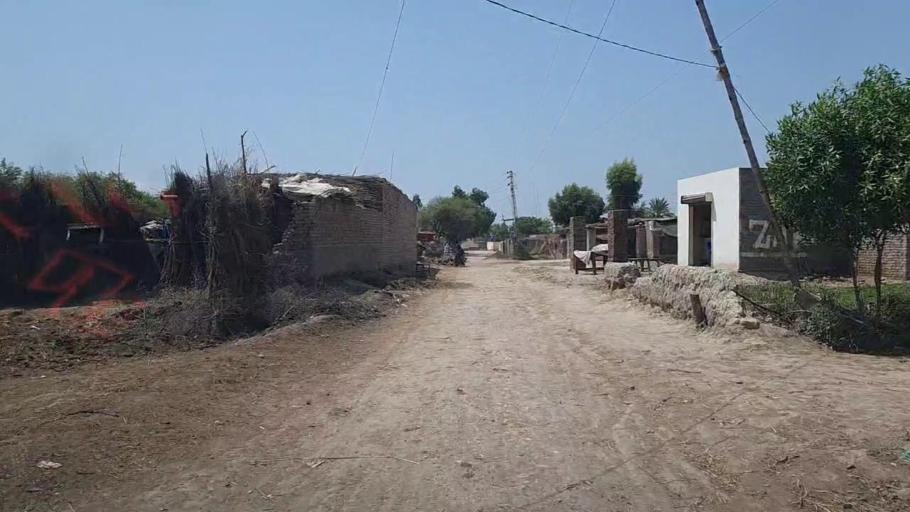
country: PK
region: Sindh
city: Ubauro
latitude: 28.1944
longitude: 69.8005
